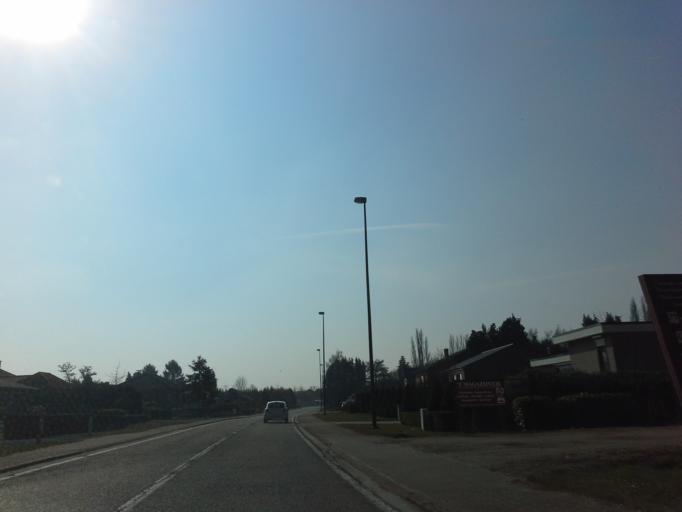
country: BE
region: Flanders
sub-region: Provincie Limburg
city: Tessenderlo
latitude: 51.0887
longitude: 5.1066
